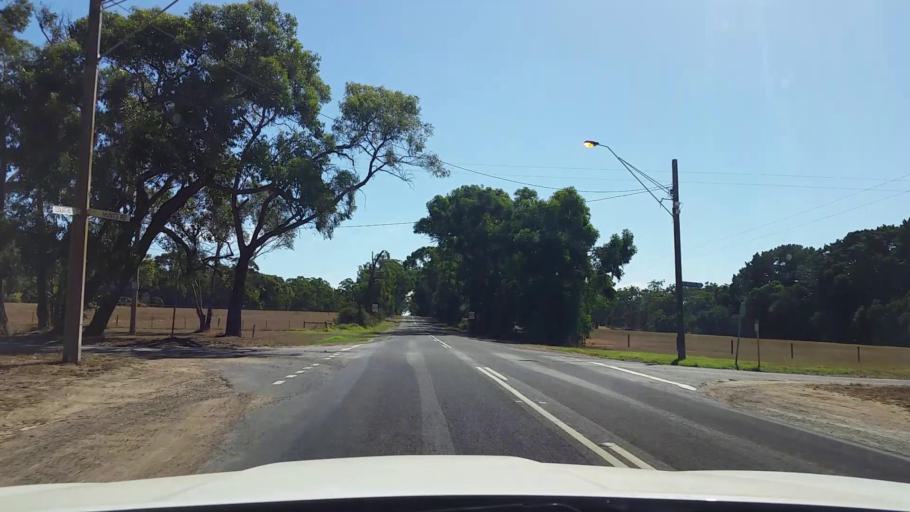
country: AU
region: Victoria
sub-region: Mornington Peninsula
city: Balnarring
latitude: -38.3244
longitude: 145.1457
